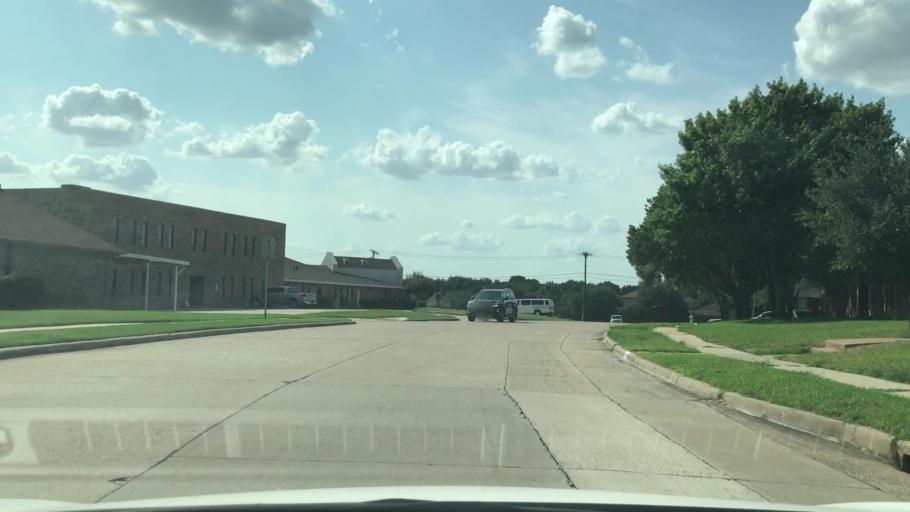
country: US
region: Texas
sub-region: Dallas County
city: Carrollton
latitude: 32.9814
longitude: -96.8686
